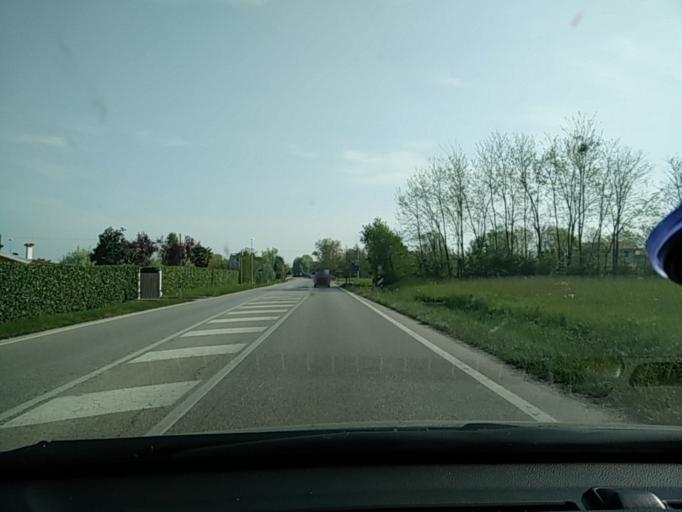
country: IT
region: Friuli Venezia Giulia
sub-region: Provincia di Pordenone
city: Azzano Decimo
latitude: 45.9238
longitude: 12.6392
